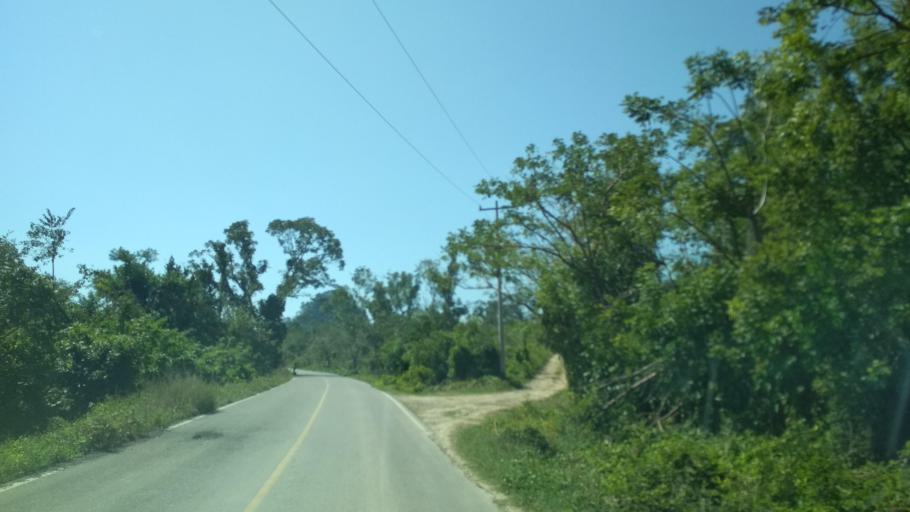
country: MX
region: Veracruz
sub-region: Papantla
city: Polutla
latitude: 20.4715
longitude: -97.2197
